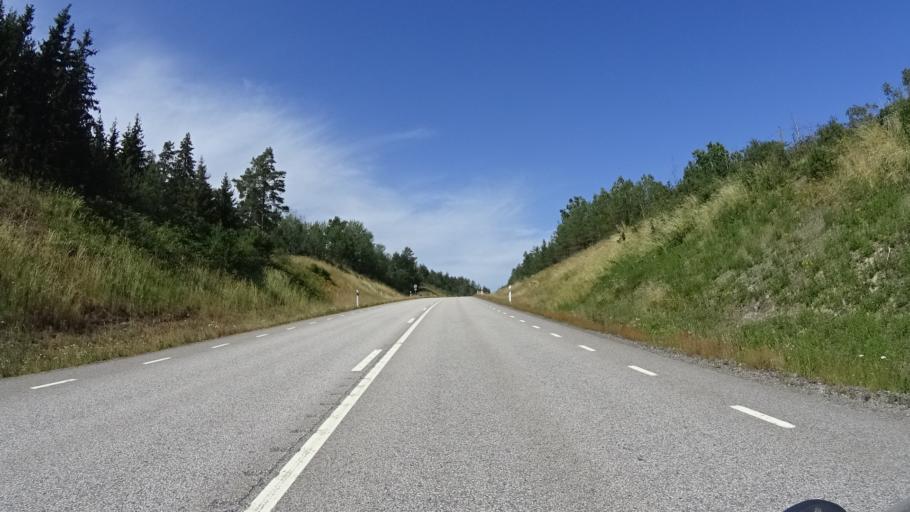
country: SE
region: Kalmar
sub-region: Vasterviks Kommun
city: Gamleby
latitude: 57.9210
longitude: 16.3746
